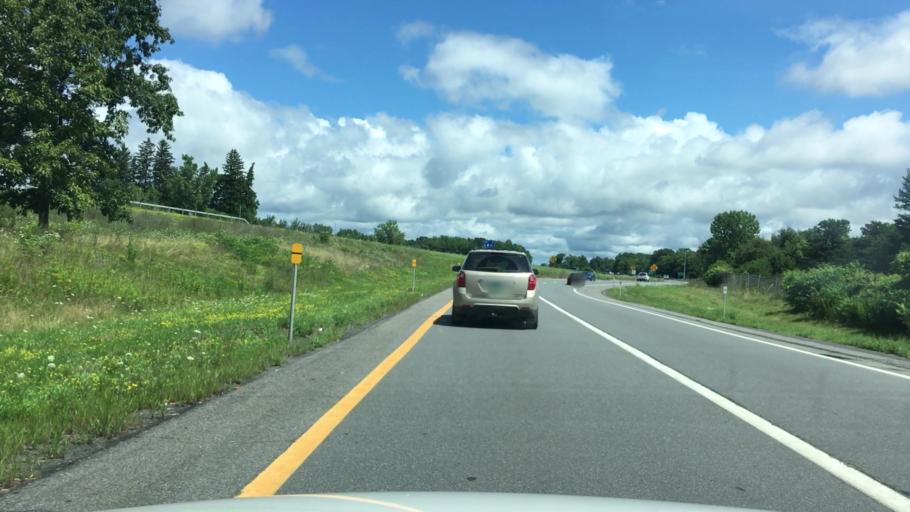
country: US
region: New York
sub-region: Albany County
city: Roessleville
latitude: 42.7281
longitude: -73.7941
